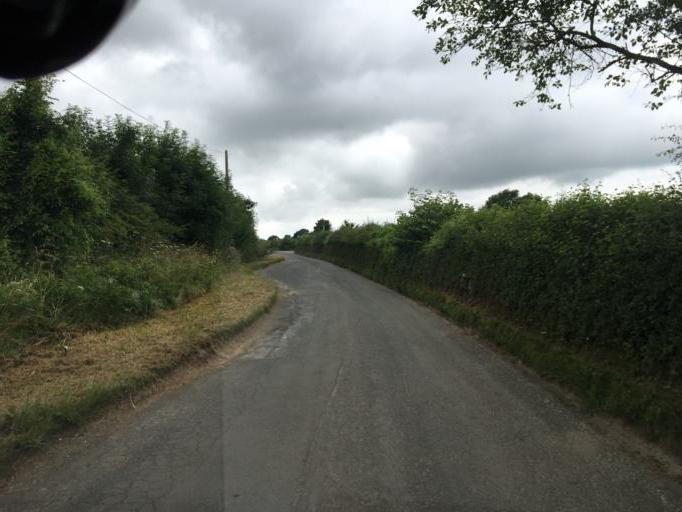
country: GB
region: England
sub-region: Gloucestershire
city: Nailsworth
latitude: 51.6998
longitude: -2.2471
